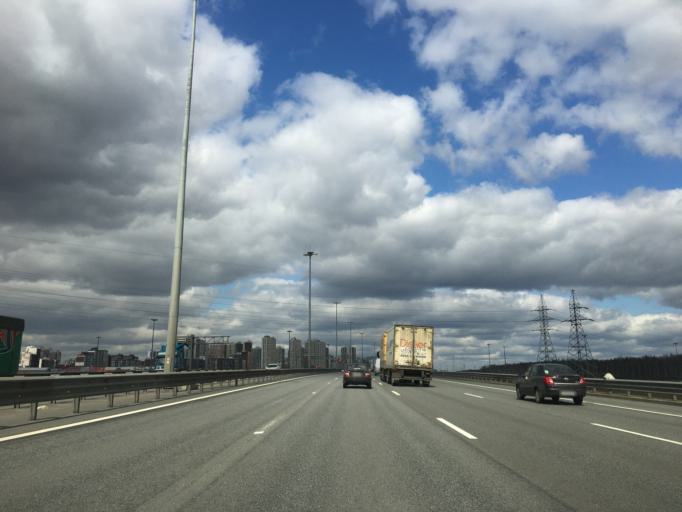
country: RU
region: Leningrad
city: Rybatskoye
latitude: 59.8888
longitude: 30.5243
